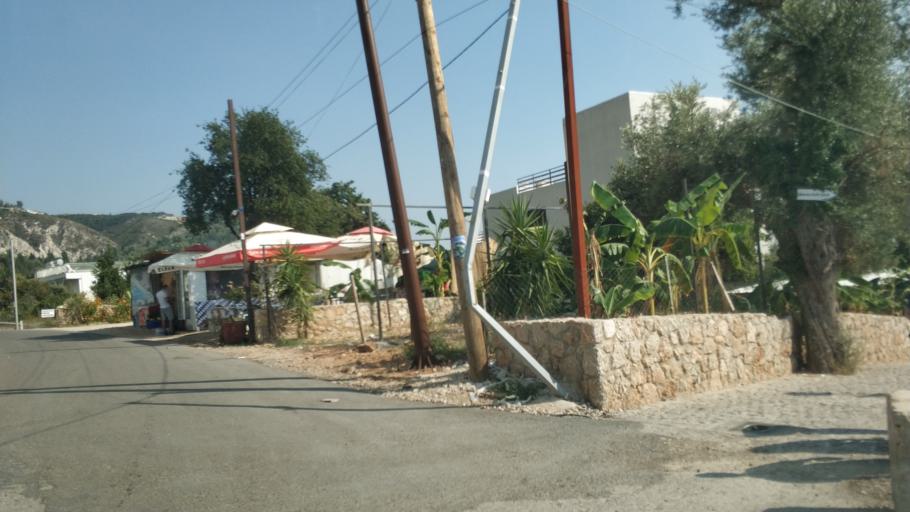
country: AL
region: Vlore
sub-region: Rrethi i Vlores
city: Vranisht
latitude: 40.1450
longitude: 19.6340
